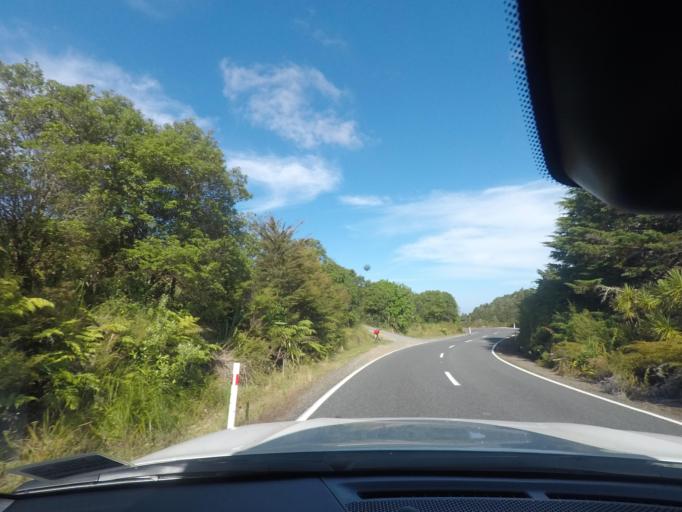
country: NZ
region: Northland
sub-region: Whangarei
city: Ngunguru
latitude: -35.6713
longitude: 174.4688
